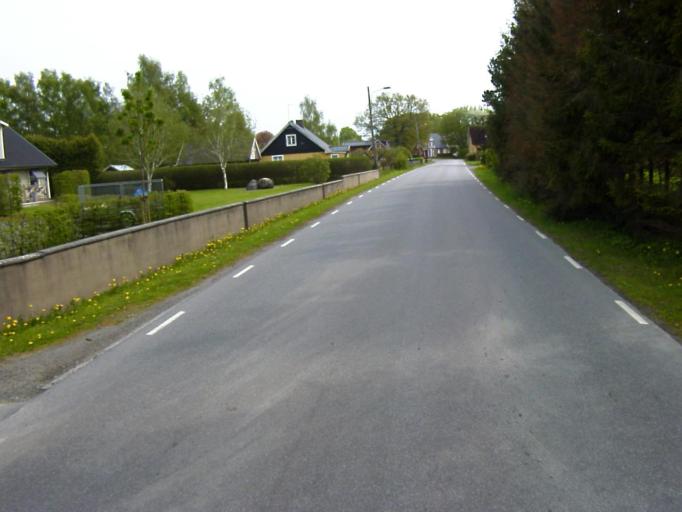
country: SE
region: Skane
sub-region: Kristianstads Kommun
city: Onnestad
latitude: 55.9382
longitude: 13.9545
